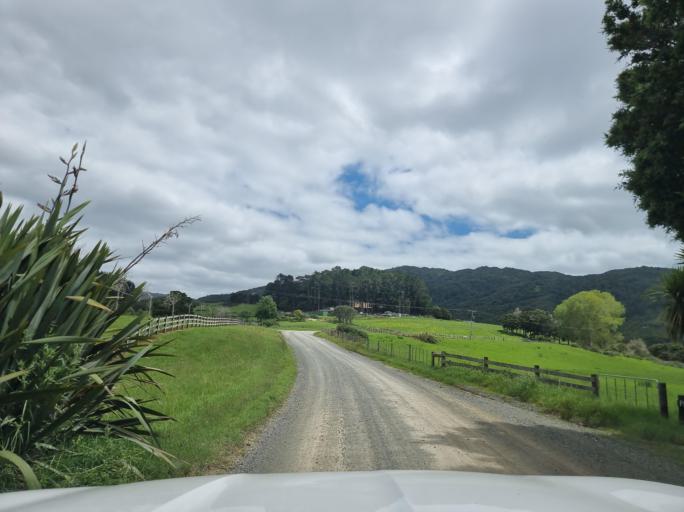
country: NZ
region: Northland
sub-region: Whangarei
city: Ruakaka
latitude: -36.0828
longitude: 174.5510
